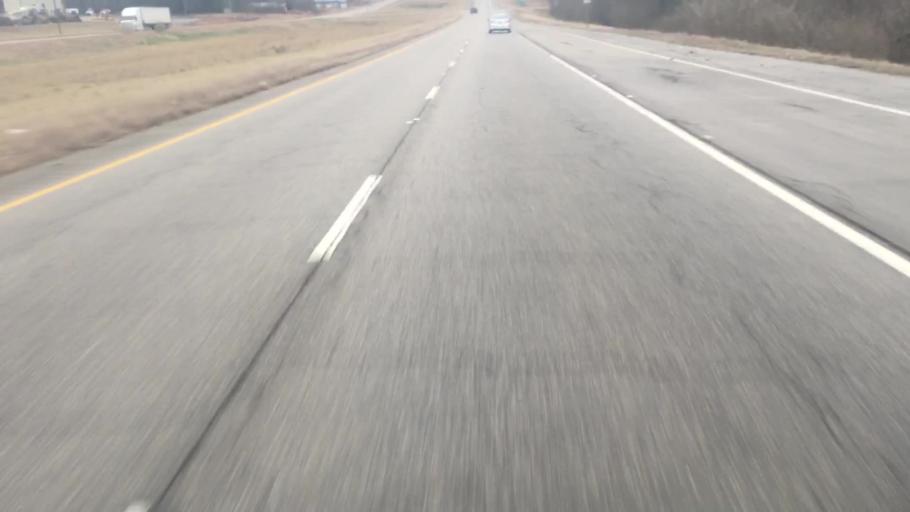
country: US
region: Alabama
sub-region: Walker County
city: Cordova
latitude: 33.8050
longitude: -87.1333
